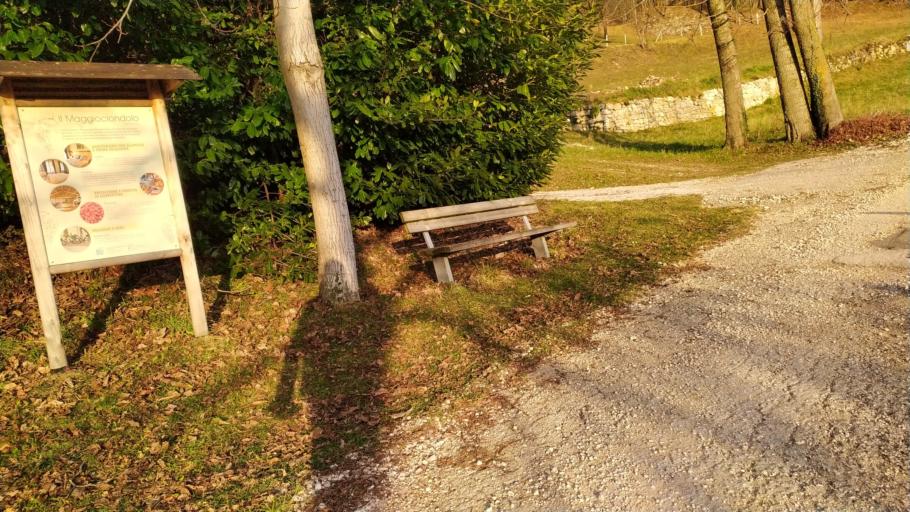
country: IT
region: Veneto
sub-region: Provincia di Vicenza
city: Velo d'Astico
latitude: 45.7627
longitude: 11.3670
